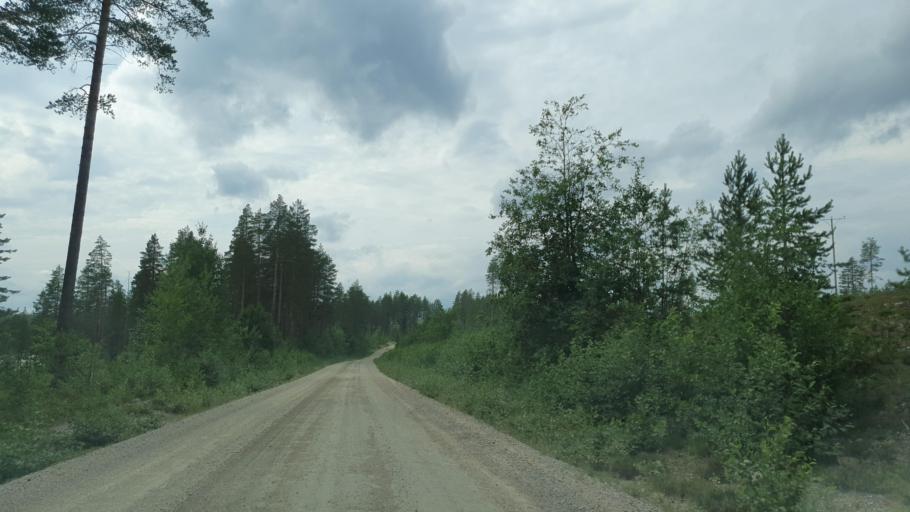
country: FI
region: Kainuu
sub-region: Kehys-Kainuu
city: Kuhmo
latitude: 64.7244
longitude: 29.6969
